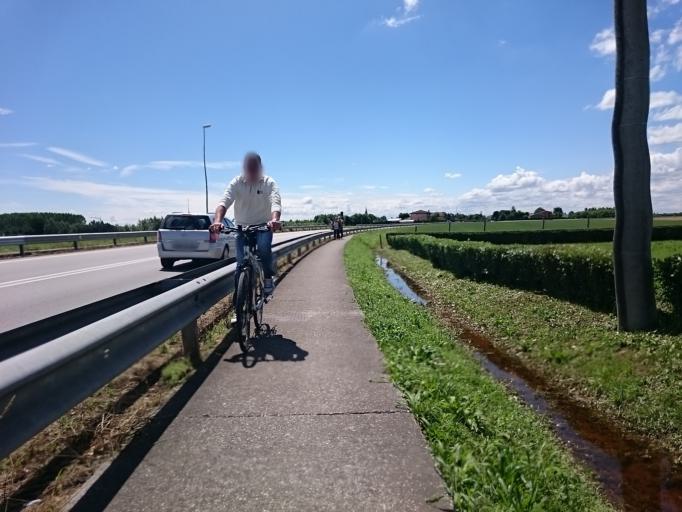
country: IT
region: Veneto
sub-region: Provincia di Padova
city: Brugine
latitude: 45.2913
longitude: 11.9978
